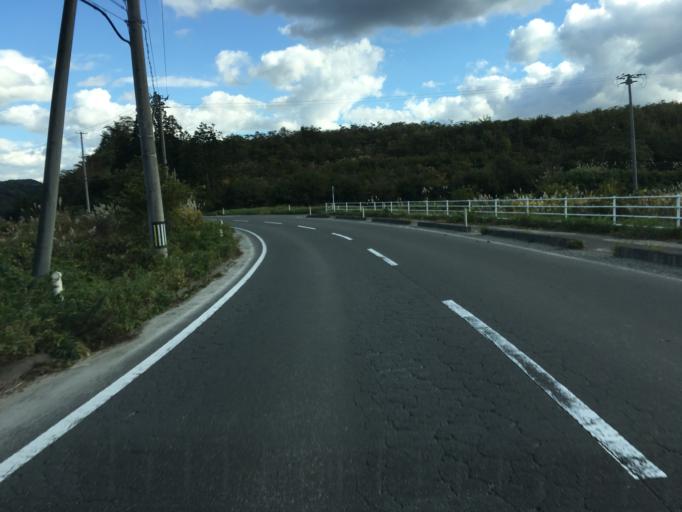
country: JP
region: Miyagi
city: Marumori
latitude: 37.8325
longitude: 140.8285
